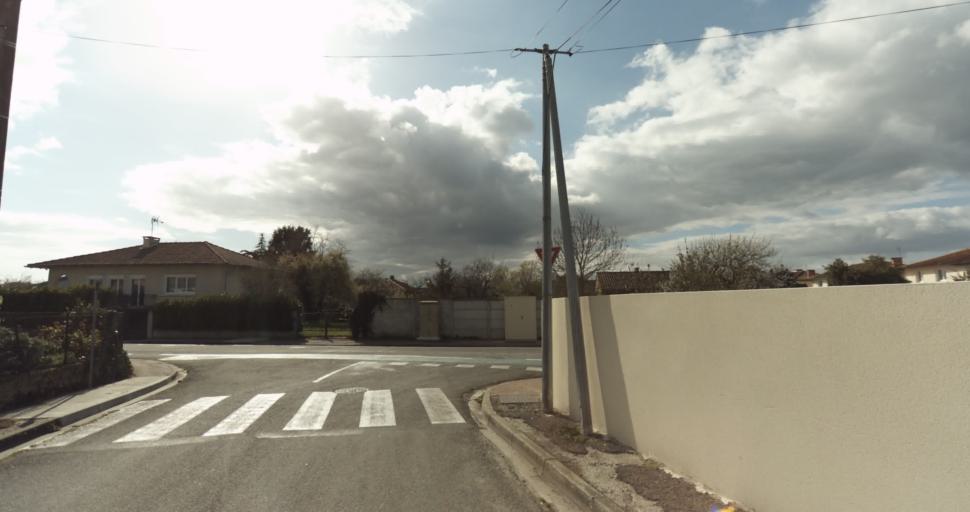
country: FR
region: Midi-Pyrenees
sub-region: Departement de la Haute-Garonne
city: Auterive
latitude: 43.3474
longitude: 1.4825
